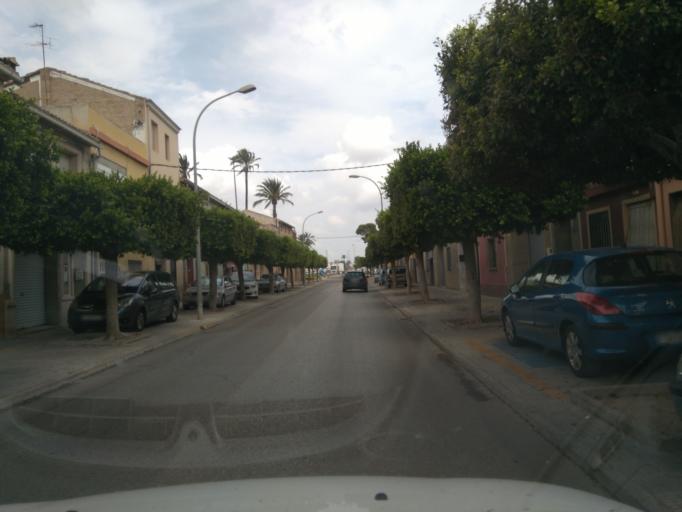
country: ES
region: Valencia
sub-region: Provincia de Valencia
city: Carcaixent
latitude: 39.1286
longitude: -0.4491
